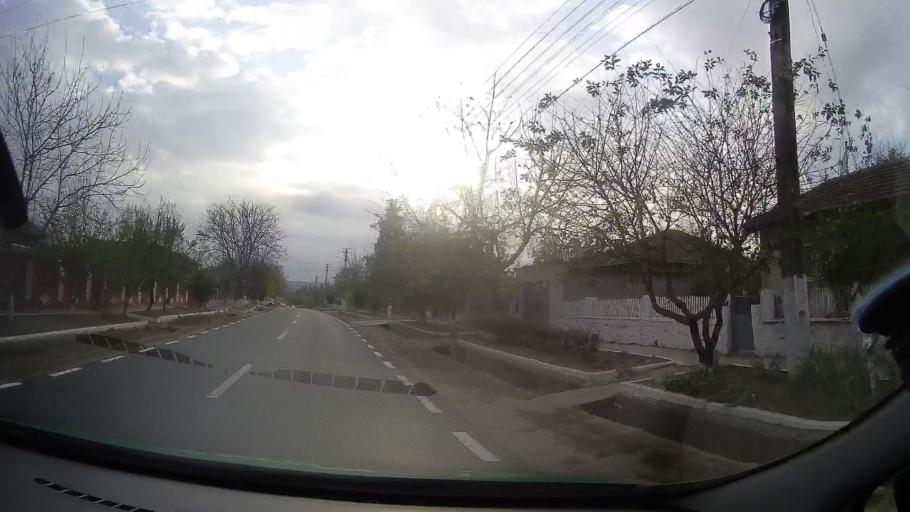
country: RO
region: Constanta
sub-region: Comuna Mircea Voda
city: Mircea Voda
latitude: 44.2788
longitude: 28.1741
